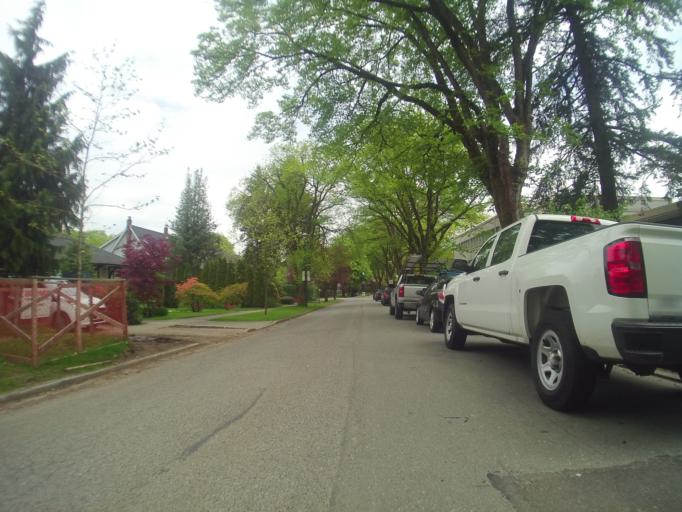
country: CA
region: British Columbia
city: Vancouver
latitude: 49.2474
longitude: -123.1381
